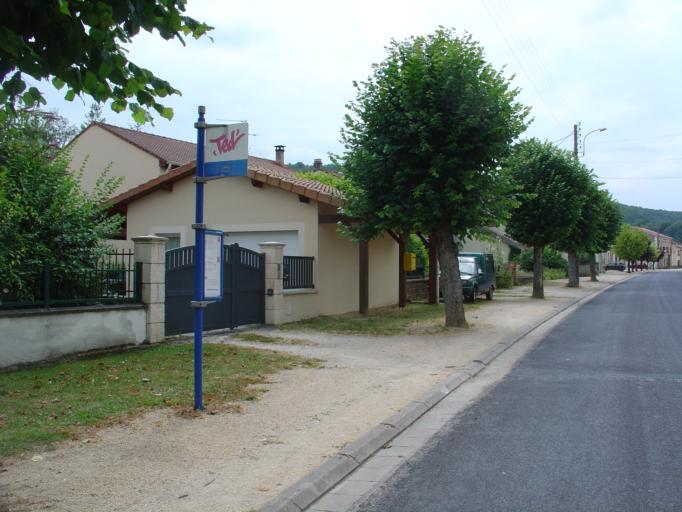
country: FR
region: Lorraine
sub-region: Departement de Meurthe-et-Moselle
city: Ecrouves
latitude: 48.7237
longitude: 5.8430
